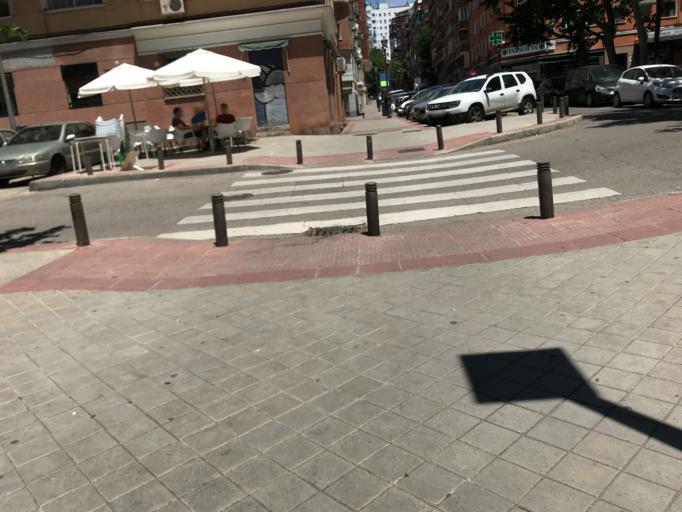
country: ES
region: Madrid
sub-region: Provincia de Madrid
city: Arganzuela
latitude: 40.3976
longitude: -3.6997
